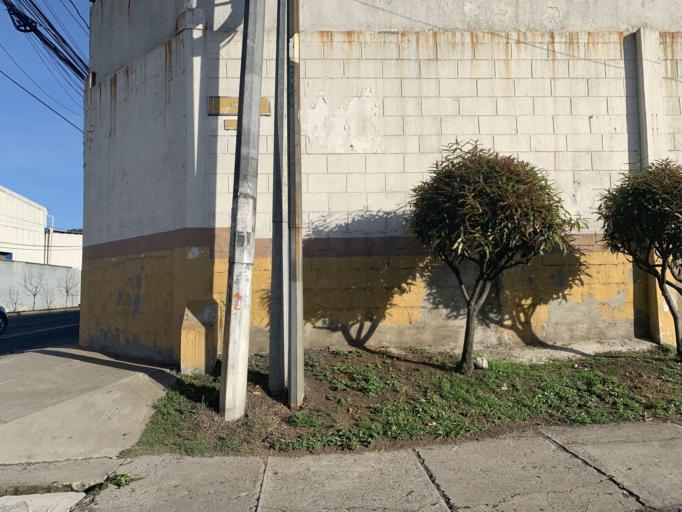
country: GT
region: Guatemala
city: Mixco
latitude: 14.5920
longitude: -90.5608
